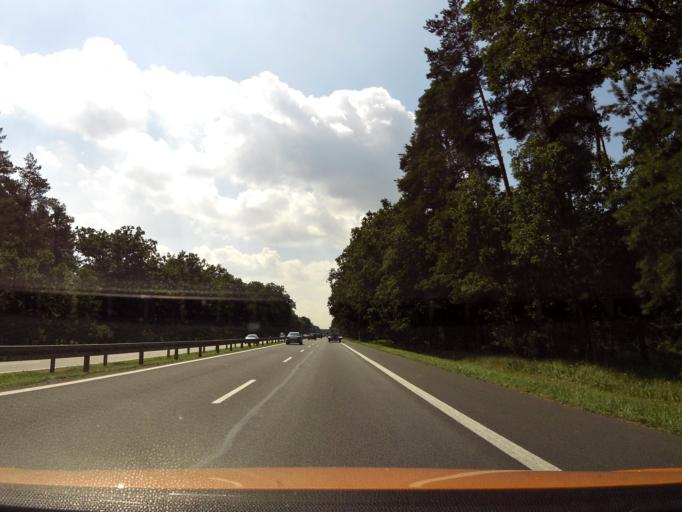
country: PL
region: West Pomeranian Voivodeship
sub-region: Powiat goleniowski
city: Goleniow
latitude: 53.4406
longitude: 14.7794
